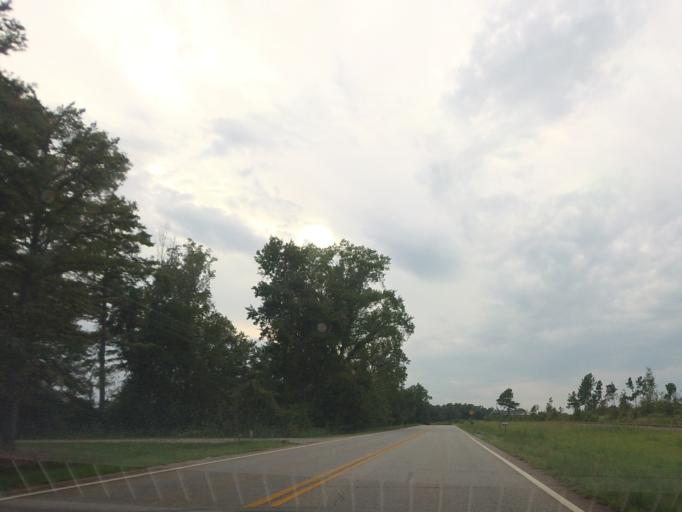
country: US
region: Georgia
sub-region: Twiggs County
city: Jeffersonville
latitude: 32.7180
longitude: -83.3977
